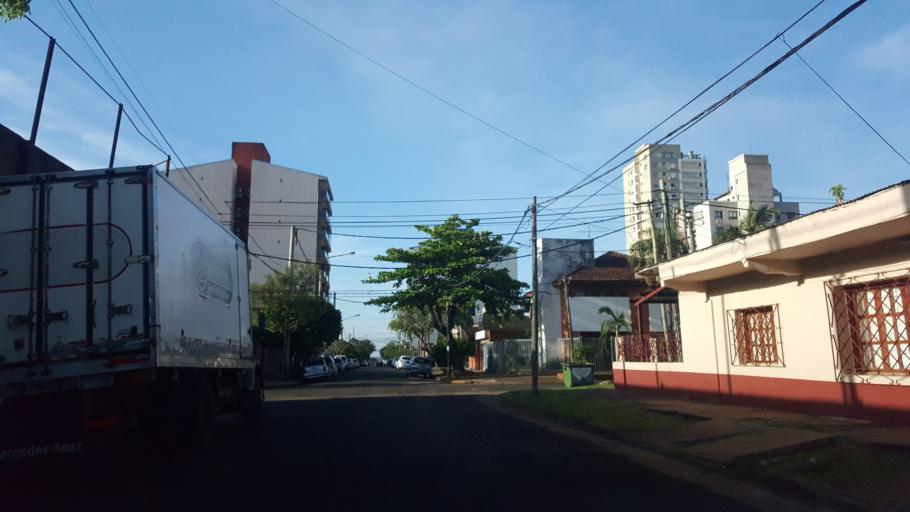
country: AR
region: Misiones
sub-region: Departamento de Capital
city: Posadas
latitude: -27.3565
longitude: -55.8953
